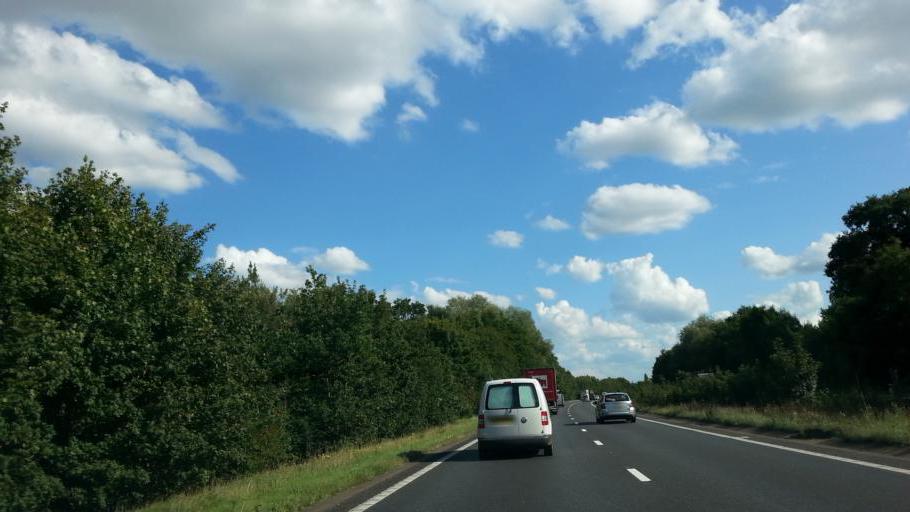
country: GB
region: England
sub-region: Suffolk
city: Needham Market
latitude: 52.1299
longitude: 1.0956
